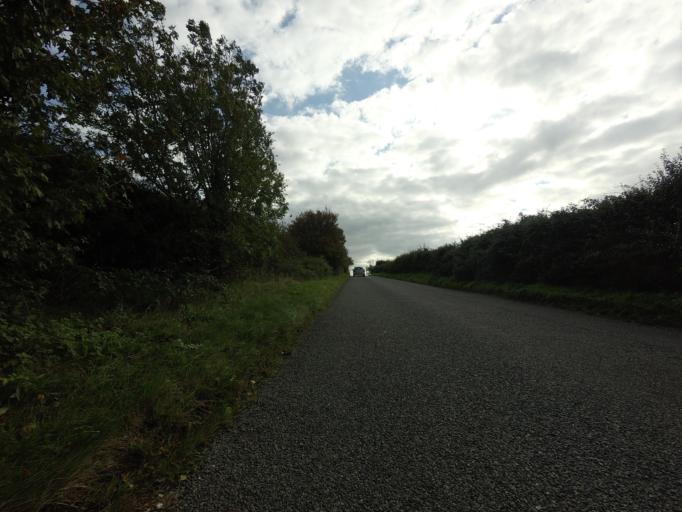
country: GB
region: England
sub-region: Norfolk
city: Snettisham
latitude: 52.9036
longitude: 0.5436
